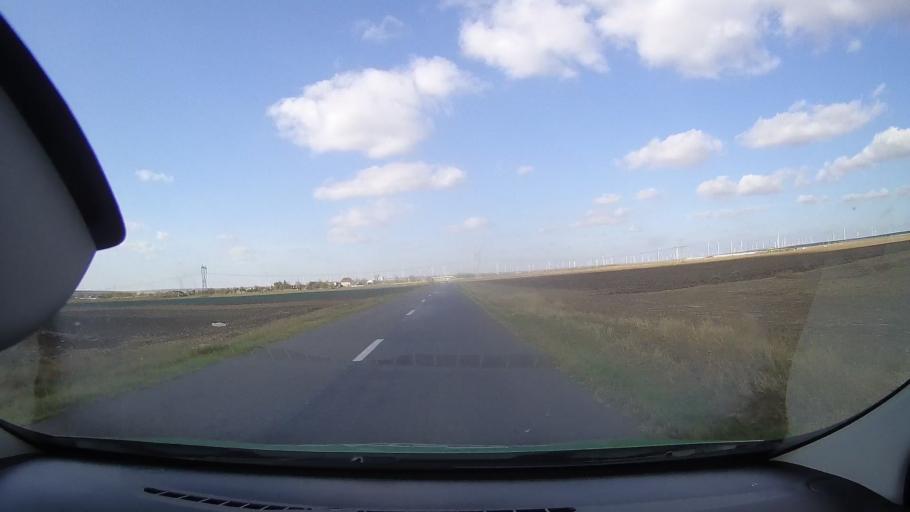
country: RO
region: Constanta
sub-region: Comuna Cogealac
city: Tariverde
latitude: 44.5557
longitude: 28.6177
